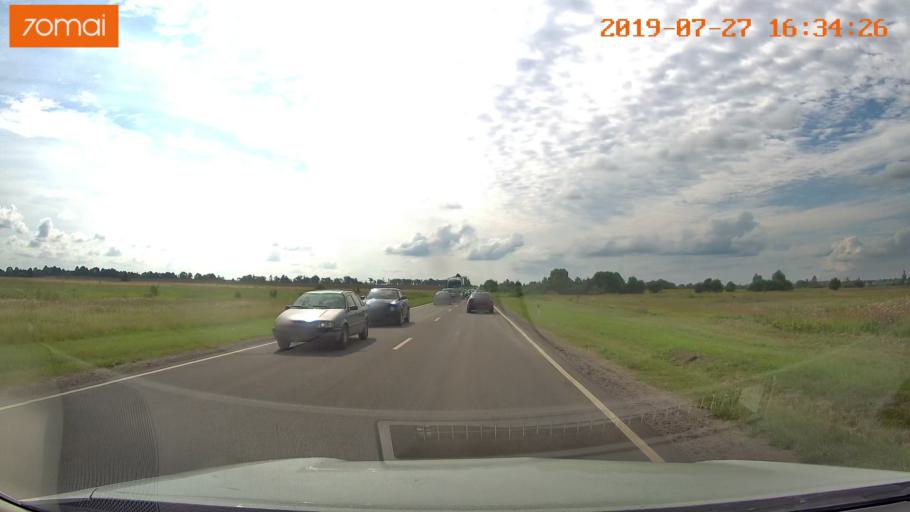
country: RU
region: Kaliningrad
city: Gvardeysk
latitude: 54.6501
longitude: 21.3265
